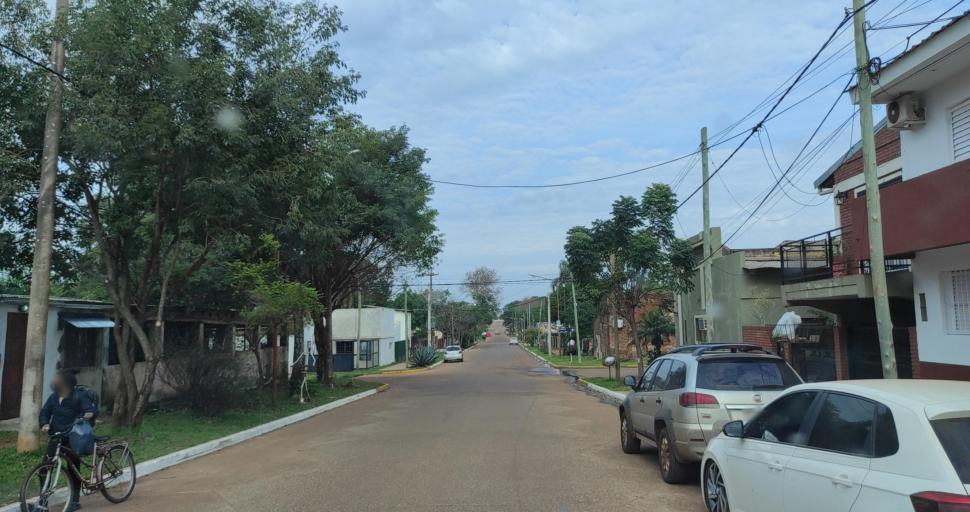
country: AR
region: Corrientes
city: Santo Tome
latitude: -28.5522
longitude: -56.0369
